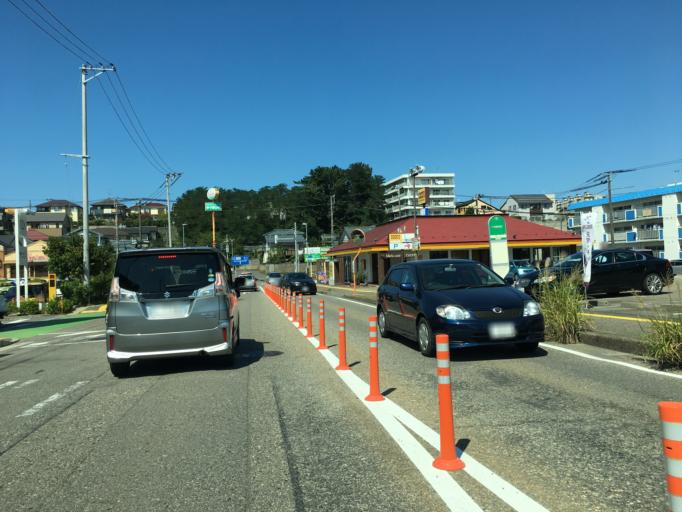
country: JP
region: Niigata
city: Niigata-shi
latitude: 37.8969
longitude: 139.0059
